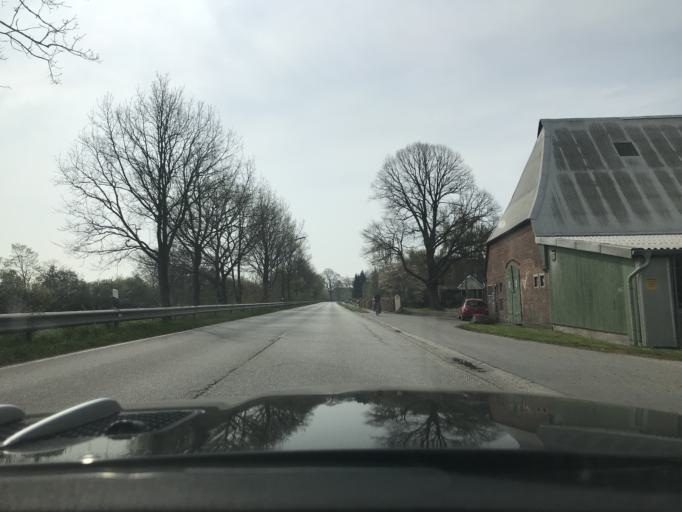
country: DE
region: Schleswig-Holstein
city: Grube
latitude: 54.2400
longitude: 11.0336
